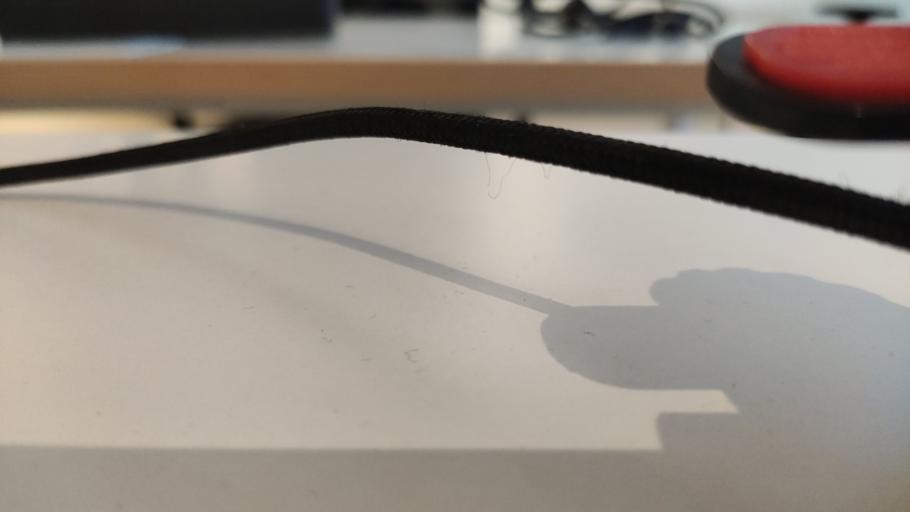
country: RU
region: Moskovskaya
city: Sychevo
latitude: 55.8397
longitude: 36.3341
